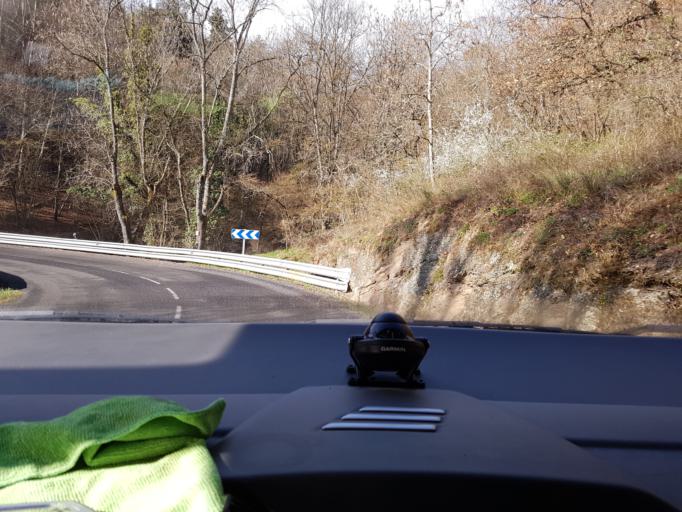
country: FR
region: Auvergne
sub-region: Departement du Cantal
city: Massiac
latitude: 45.2370
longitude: 3.1998
